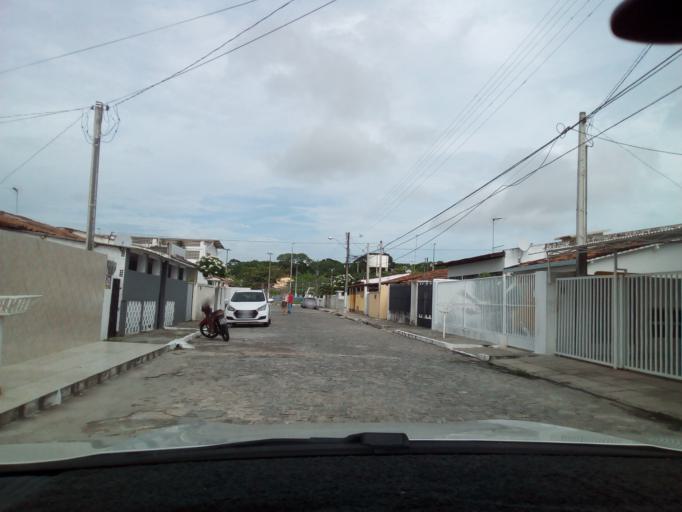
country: BR
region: Paraiba
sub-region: Joao Pessoa
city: Joao Pessoa
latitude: -7.1318
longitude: -34.8499
